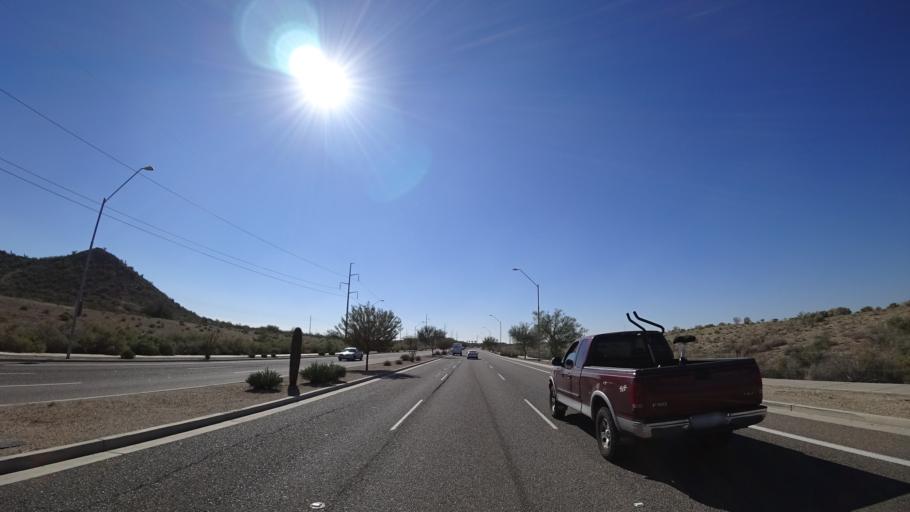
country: US
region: Arizona
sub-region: Maricopa County
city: Cave Creek
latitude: 33.6871
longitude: -112.0505
